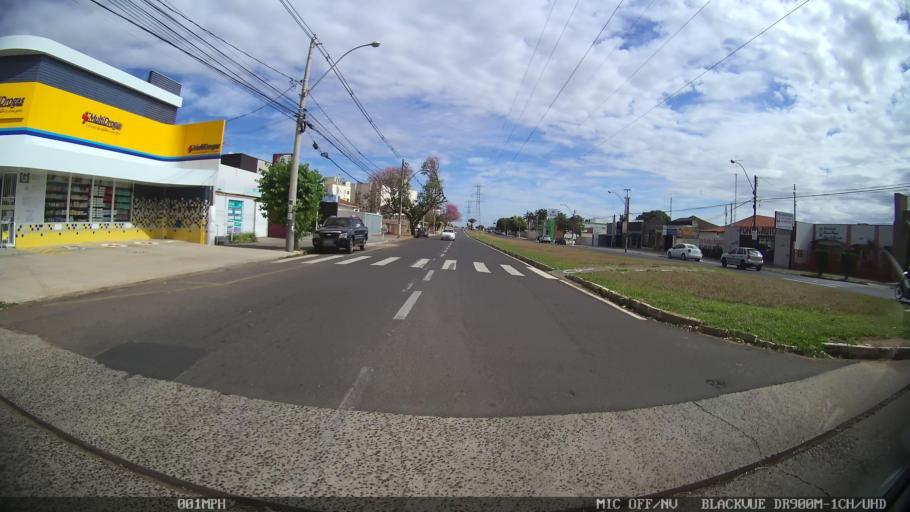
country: BR
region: Sao Paulo
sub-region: Bady Bassitt
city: Bady Bassitt
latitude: -20.8123
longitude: -49.5074
